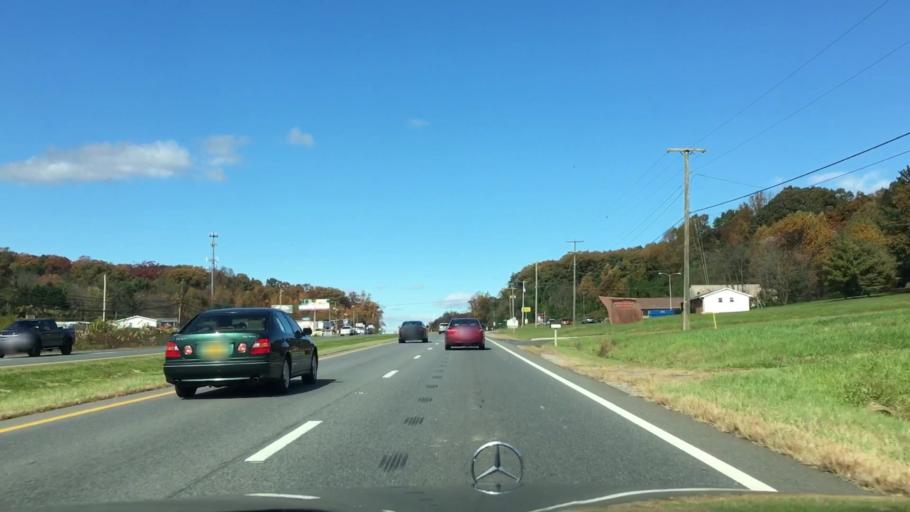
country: US
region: Virginia
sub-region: Campbell County
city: Rustburg
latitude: 37.2950
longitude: -79.1710
